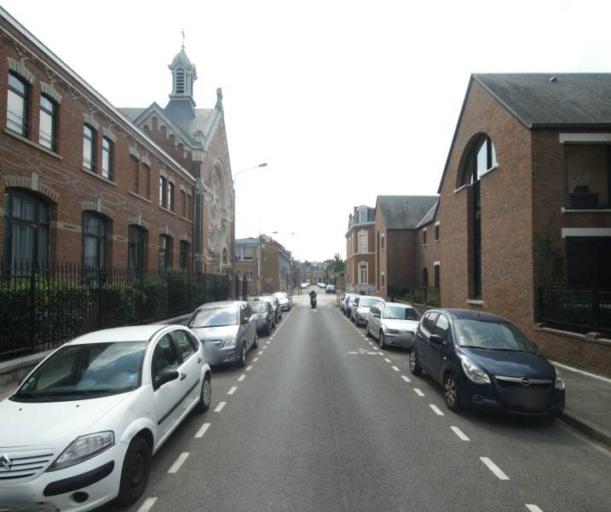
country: FR
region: Nord-Pas-de-Calais
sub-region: Departement du Nord
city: Armentieres
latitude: 50.6871
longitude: 2.8753
